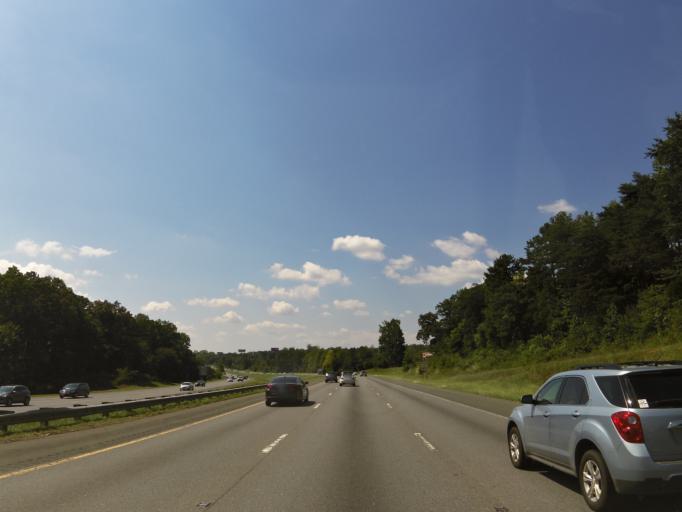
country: US
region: North Carolina
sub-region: Gaston County
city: Belmont
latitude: 35.2623
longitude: -81.0538
